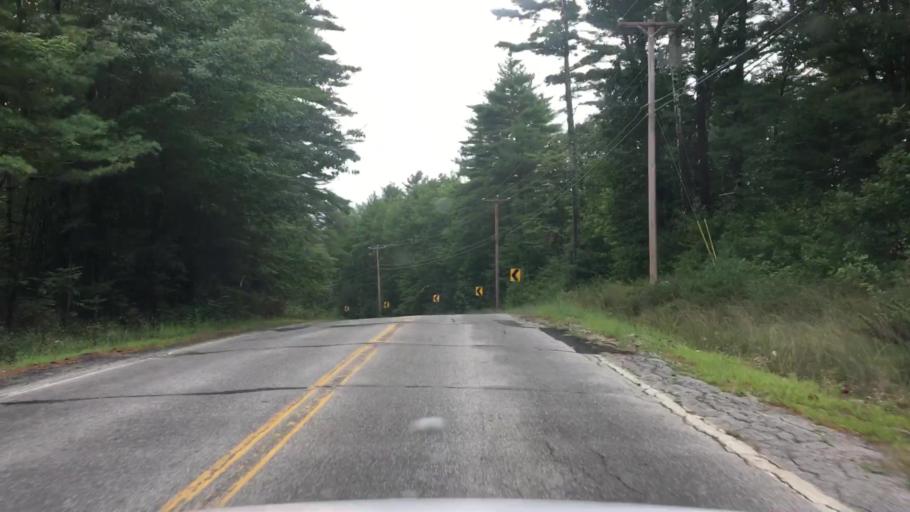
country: US
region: Maine
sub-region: York County
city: Cornish
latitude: 43.8180
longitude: -70.7746
